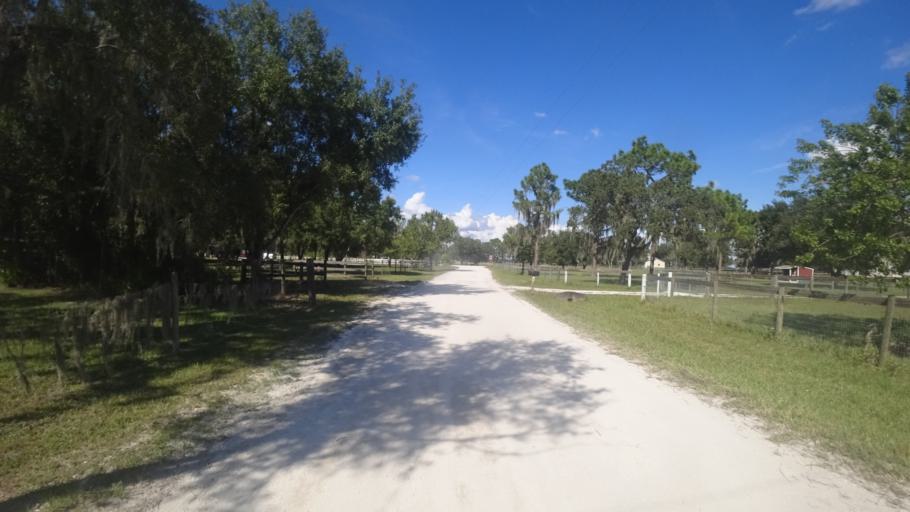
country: US
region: Florida
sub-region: Sarasota County
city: The Meadows
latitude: 27.4517
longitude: -82.2951
